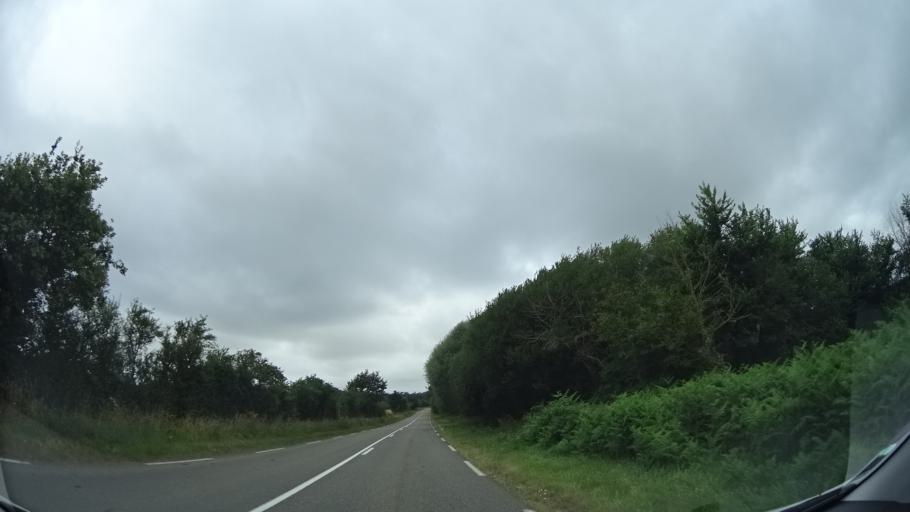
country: FR
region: Lower Normandy
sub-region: Departement de la Manche
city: Portbail
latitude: 49.3203
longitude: -1.6306
